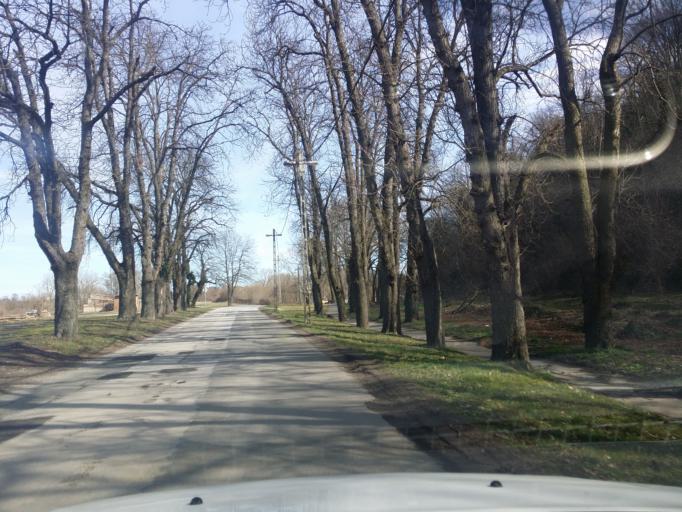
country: HU
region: Baranya
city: Villany
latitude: 45.8770
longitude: 18.4521
